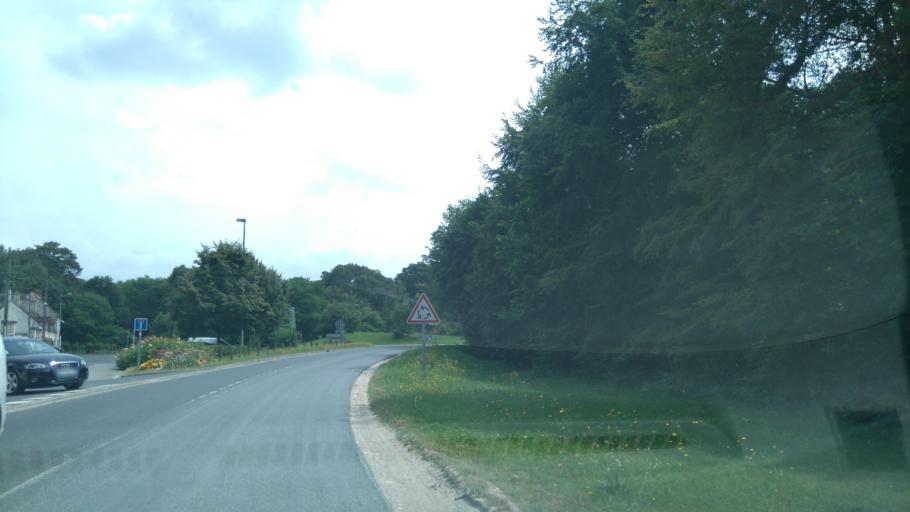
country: FR
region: Picardie
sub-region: Departement de l'Oise
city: Saint-Maximin
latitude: 49.2215
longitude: 2.4656
